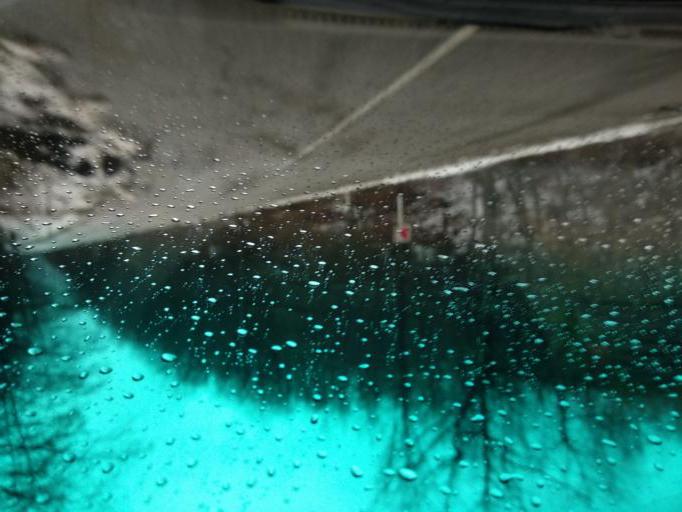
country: RU
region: Krasnodarskiy
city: Khadyzhensk
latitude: 44.2217
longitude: 39.3890
